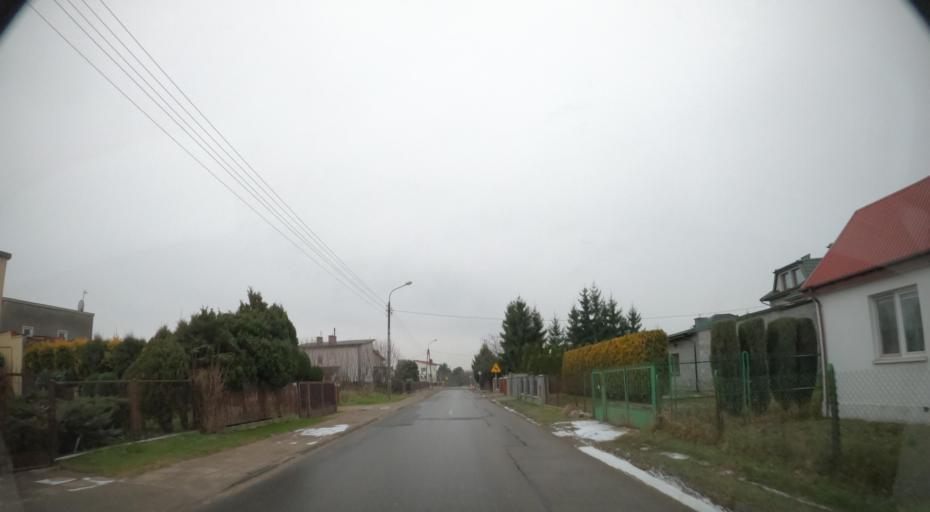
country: PL
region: Masovian Voivodeship
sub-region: Radom
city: Radom
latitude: 51.3817
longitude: 21.1943
